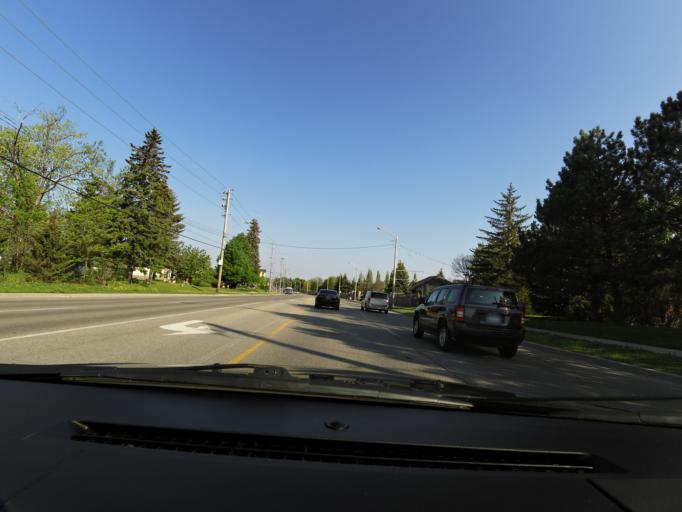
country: CA
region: Ontario
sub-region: Wellington County
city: Guelph
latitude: 43.5186
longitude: -80.2061
